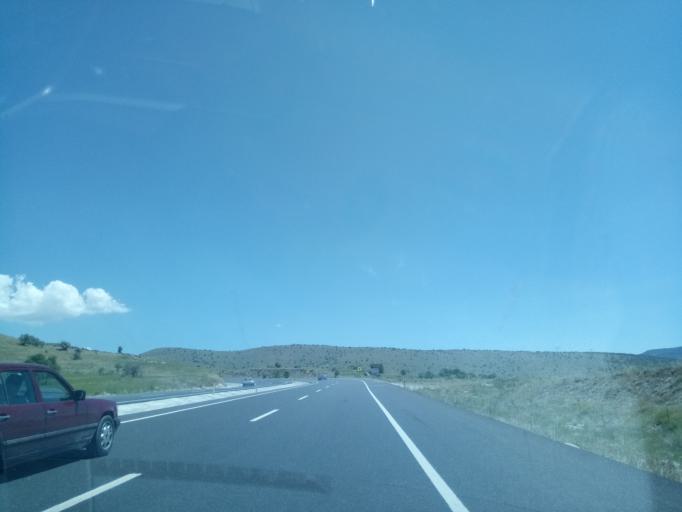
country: TR
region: Konya
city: Kiziloren
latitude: 37.7250
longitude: 32.0597
